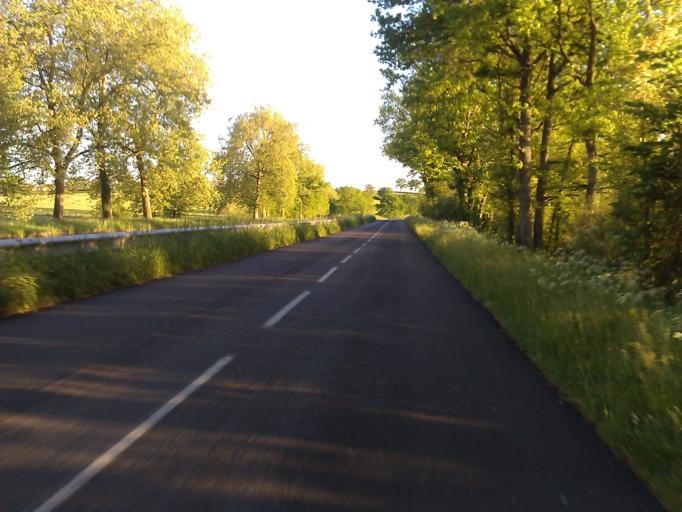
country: FR
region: Bourgogne
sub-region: Departement de Saone-et-Loire
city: Palinges
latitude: 46.5119
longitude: 4.1941
